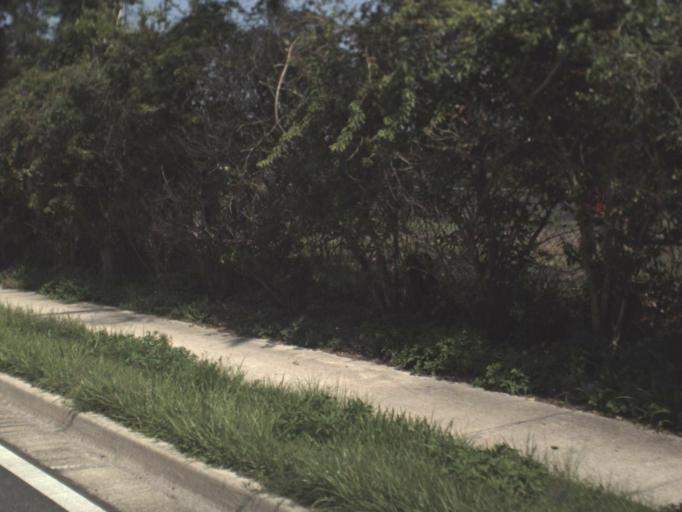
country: US
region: Florida
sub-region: Clay County
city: Bellair-Meadowbrook Terrace
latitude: 30.2475
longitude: -81.7271
